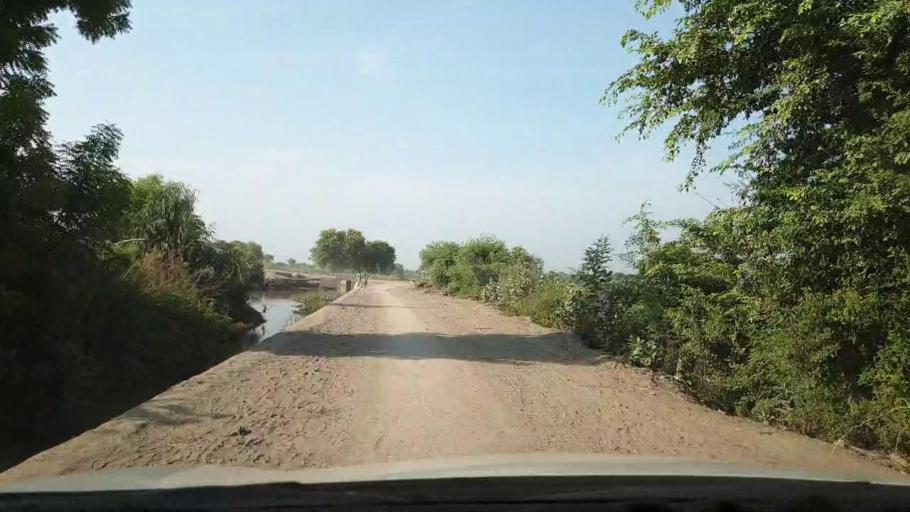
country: PK
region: Sindh
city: Larkana
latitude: 27.5460
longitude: 68.2672
